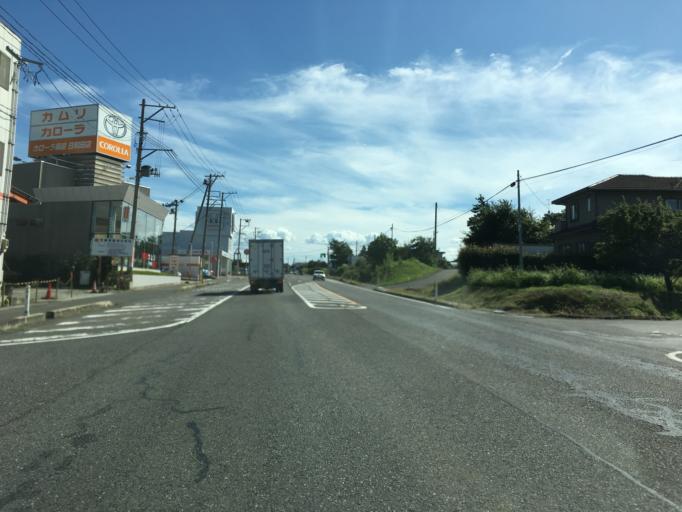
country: JP
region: Fukushima
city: Koriyama
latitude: 37.4429
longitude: 140.3796
